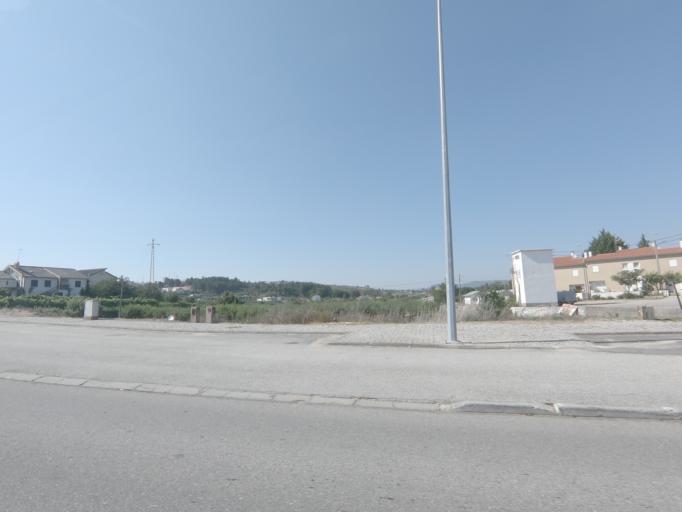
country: PT
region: Viseu
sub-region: Moimenta da Beira
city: Moimenta da Beira
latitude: 40.9805
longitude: -7.6079
